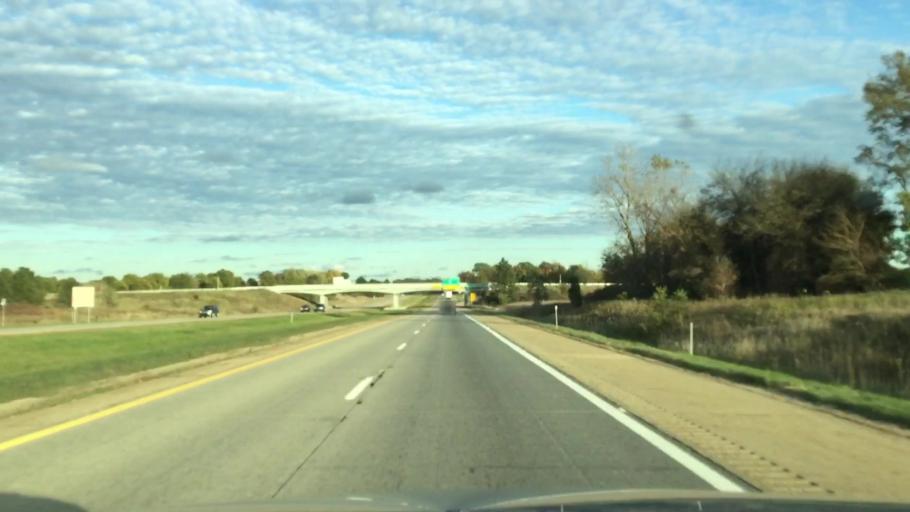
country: US
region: Michigan
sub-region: Calhoun County
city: Albion
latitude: 42.2631
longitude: -84.7118
